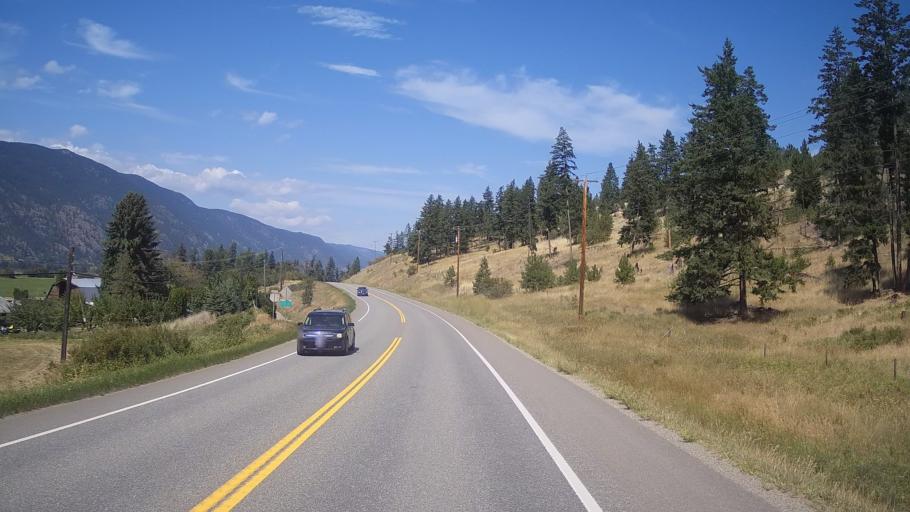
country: CA
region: British Columbia
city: Kamloops
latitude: 50.9191
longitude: -120.2353
